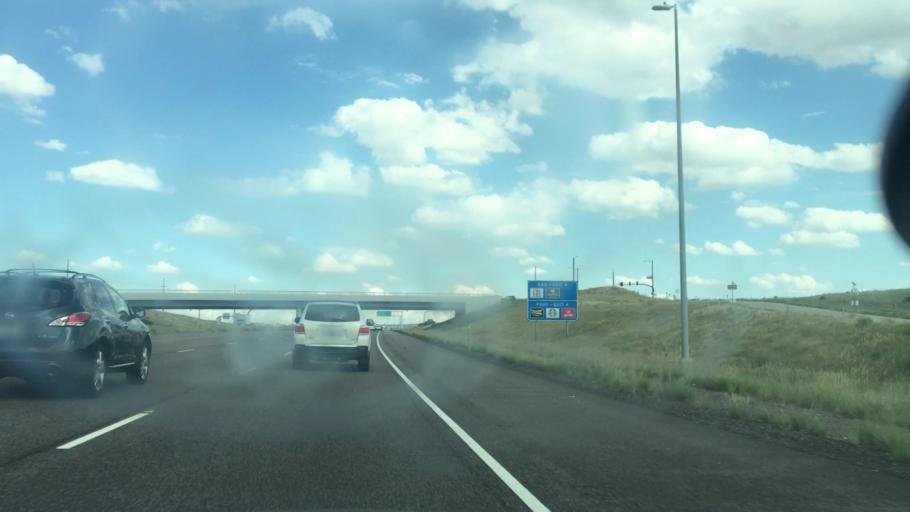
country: US
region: Colorado
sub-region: Douglas County
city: Stonegate
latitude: 39.5540
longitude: -104.8102
